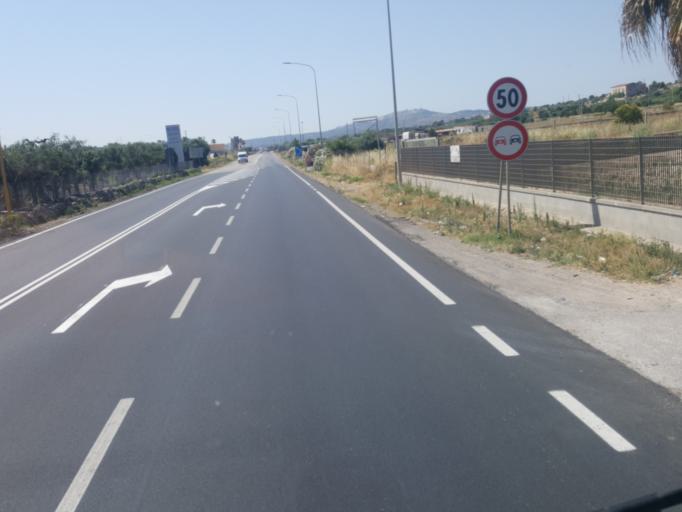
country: IT
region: Apulia
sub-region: Provincia di Taranto
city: Massafra
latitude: 40.5890
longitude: 17.1017
